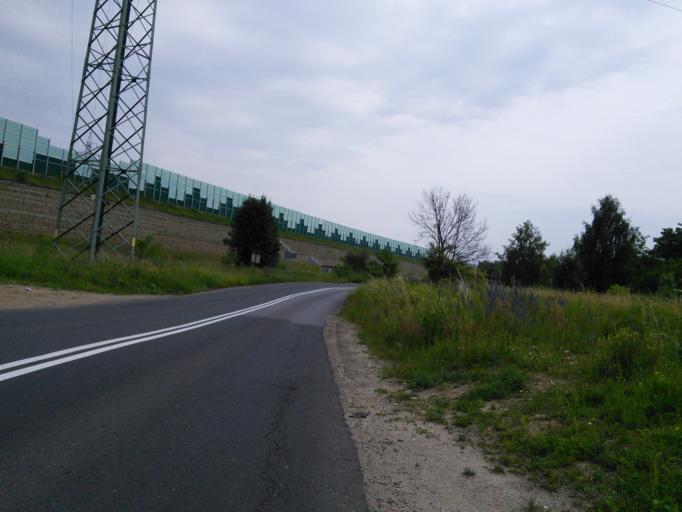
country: PL
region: Silesian Voivodeship
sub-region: Powiat bedzinski
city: Bobrowniki
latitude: 50.3741
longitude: 18.9629
